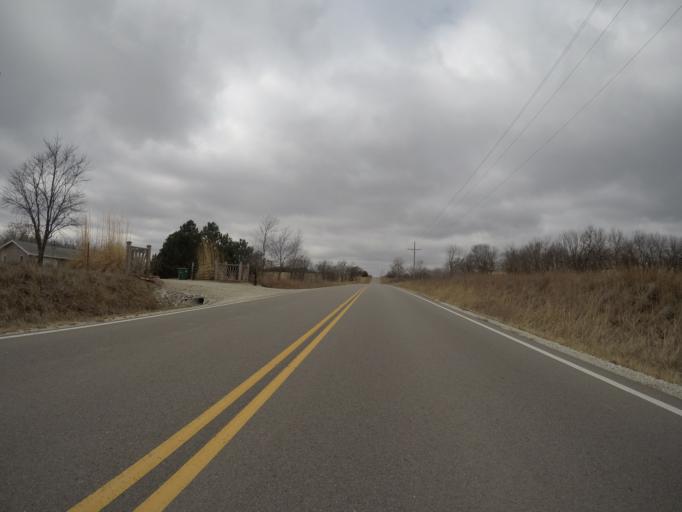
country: US
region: Kansas
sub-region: Pottawatomie County
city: Westmoreland
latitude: 39.4212
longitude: -96.4771
